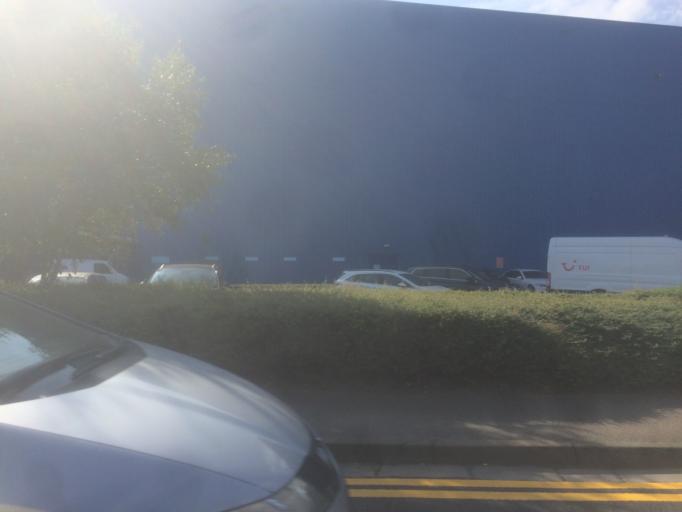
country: GB
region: England
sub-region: Luton
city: Luton
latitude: 51.8808
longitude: -0.3821
